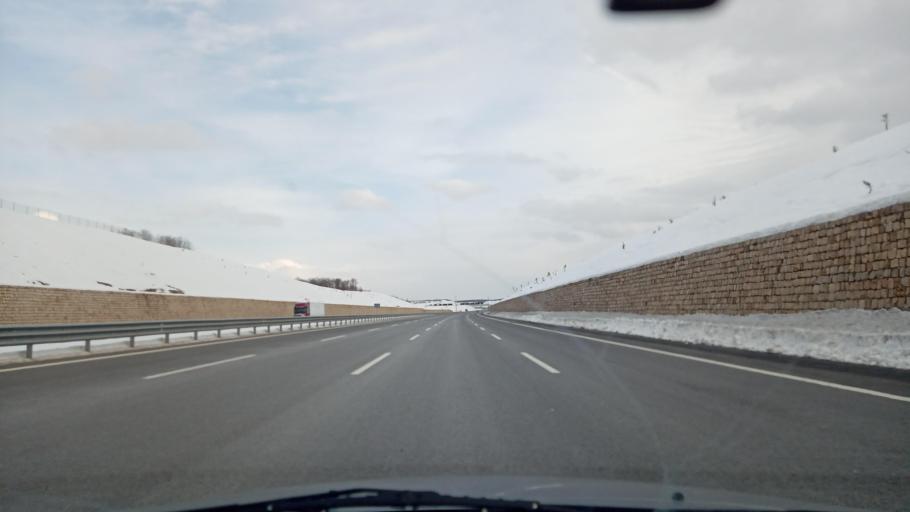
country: TR
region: Kocaeli
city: Hereke
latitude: 40.8917
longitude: 29.6013
